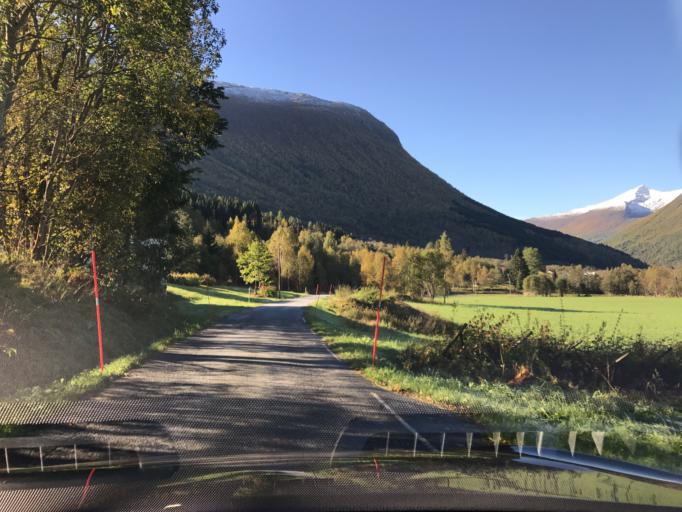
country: NO
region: More og Romsdal
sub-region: Norddal
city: Valldal
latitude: 62.3316
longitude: 7.3883
